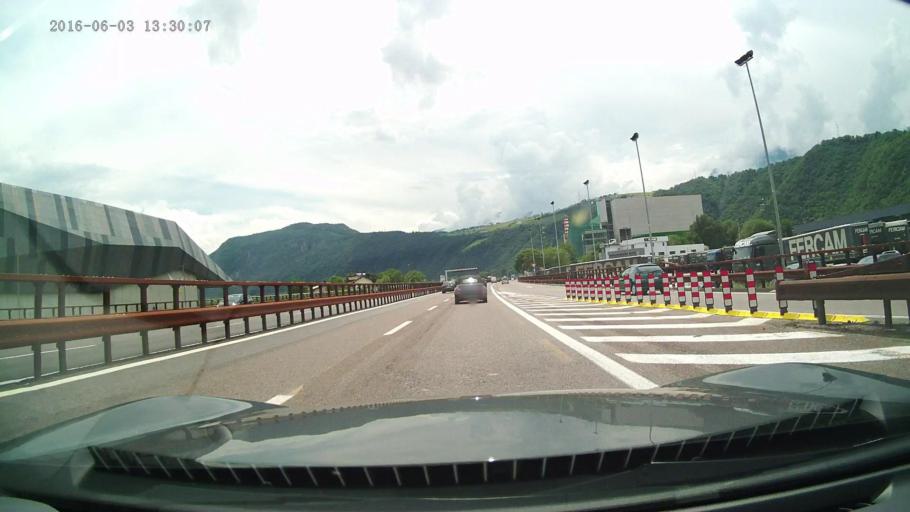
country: IT
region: Trentino-Alto Adige
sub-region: Bolzano
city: San Giacomo
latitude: 46.4704
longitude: 11.3126
